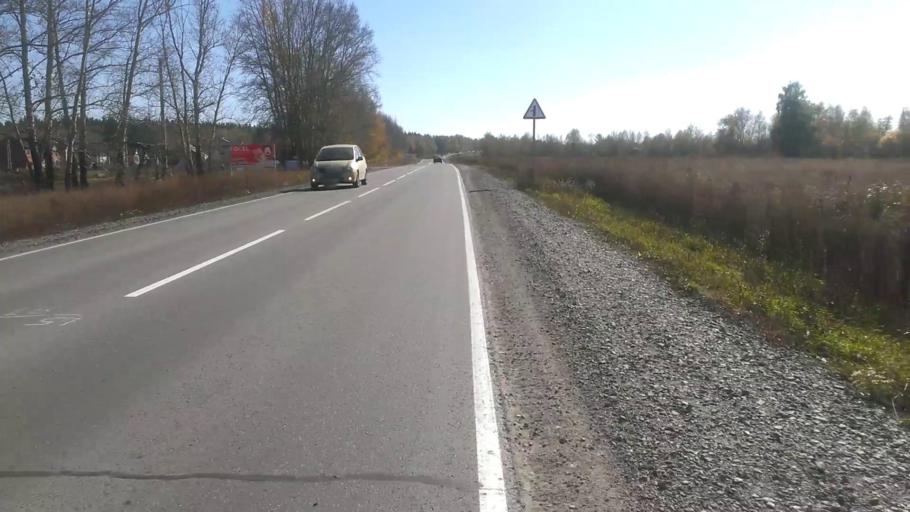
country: RU
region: Altai Krai
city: Sannikovo
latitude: 53.3079
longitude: 83.9678
